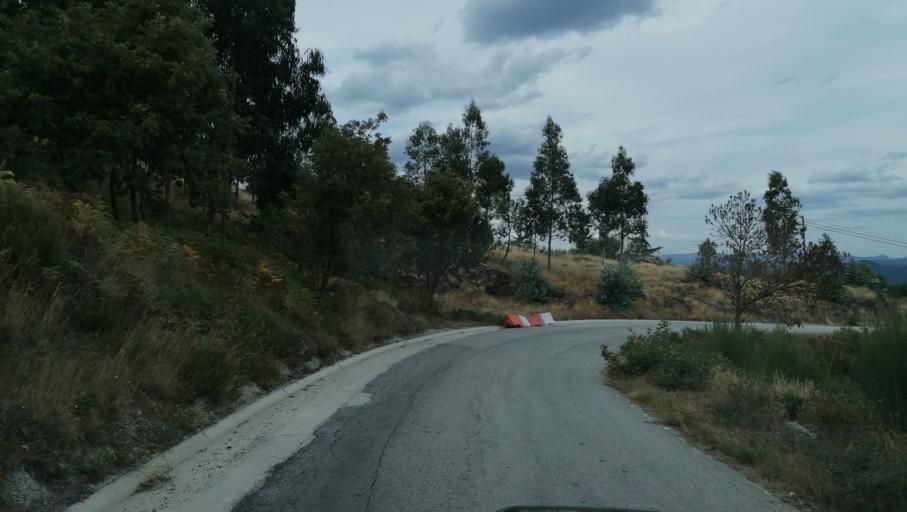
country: PT
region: Vila Real
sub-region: Vila Pouca de Aguiar
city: Vila Pouca de Aguiar
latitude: 41.5607
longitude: -7.6835
